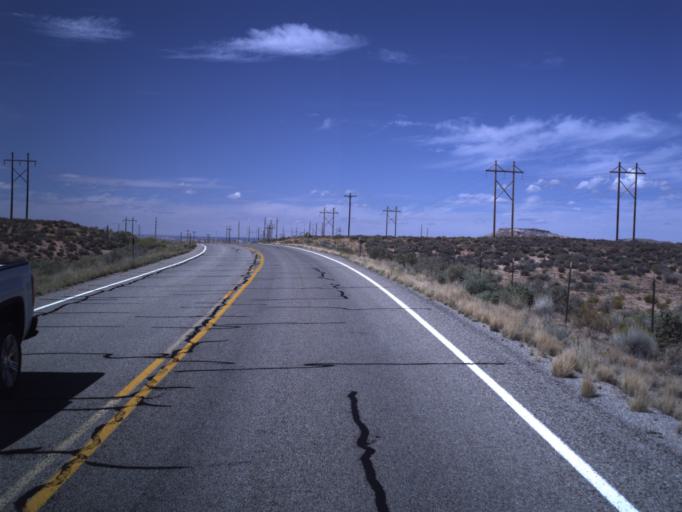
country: US
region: Utah
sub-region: San Juan County
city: Blanding
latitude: 37.2798
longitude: -109.3652
